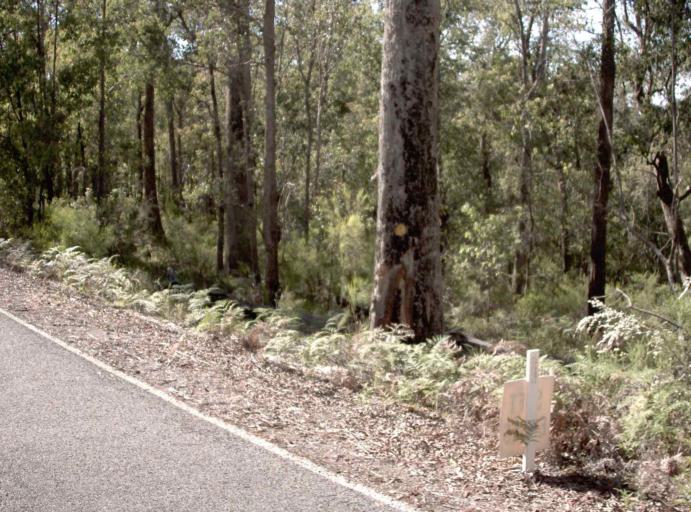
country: AU
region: New South Wales
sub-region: Bombala
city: Bombala
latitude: -37.3786
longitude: 148.6640
